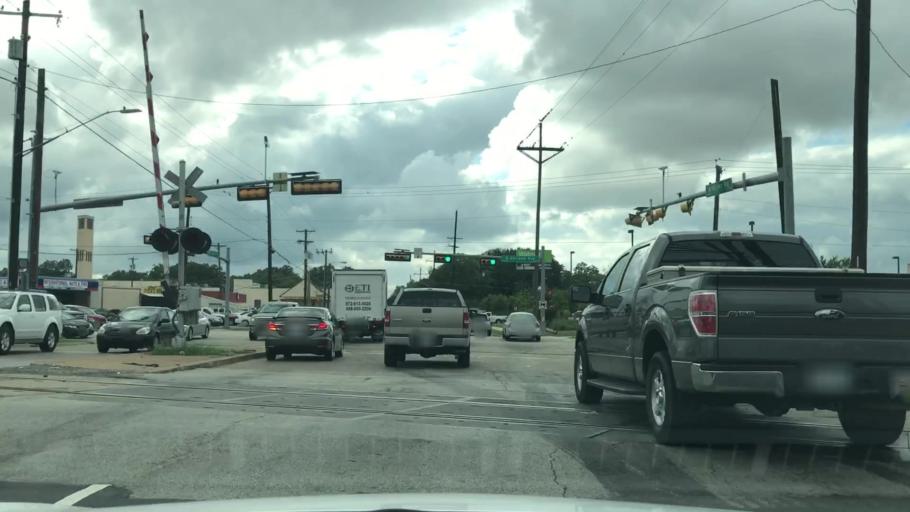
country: US
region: Texas
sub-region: Dallas County
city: Garland
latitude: 32.8944
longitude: -96.6486
